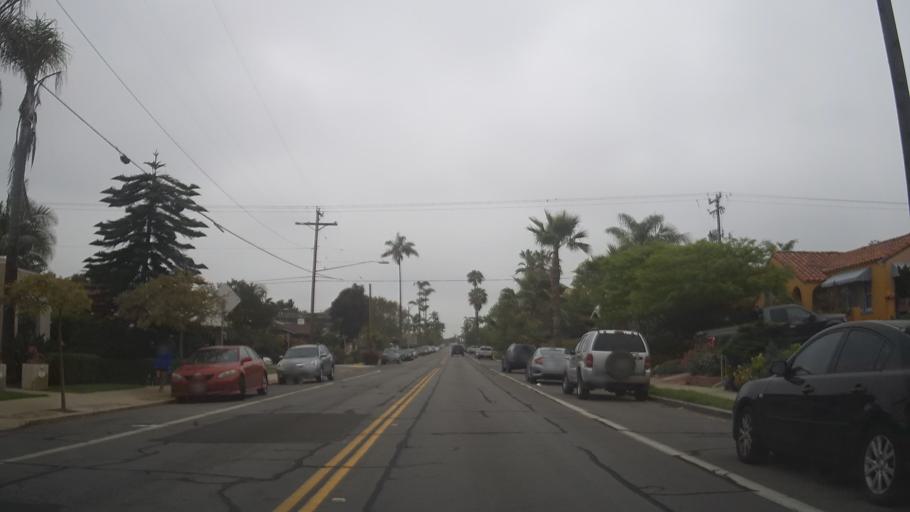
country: US
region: California
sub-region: San Diego County
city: San Diego
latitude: 32.7414
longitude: -117.1390
